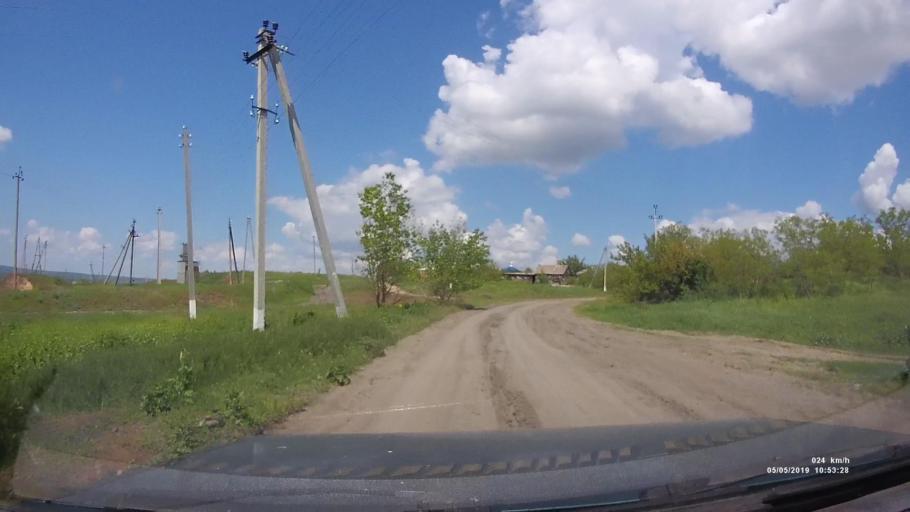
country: RU
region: Rostov
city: Ust'-Donetskiy
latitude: 47.6544
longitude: 40.8247
